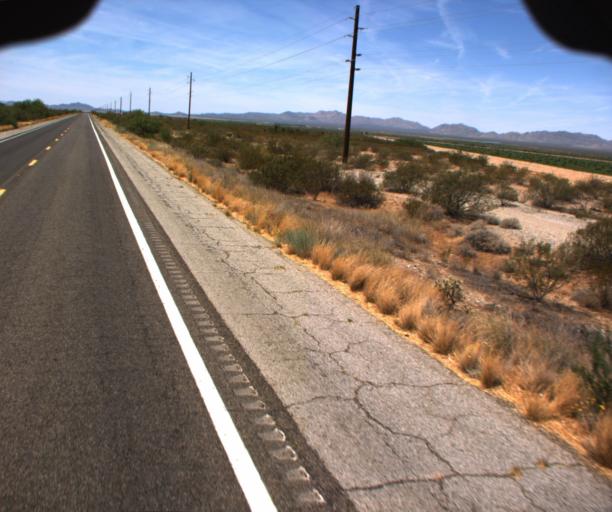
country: US
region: Arizona
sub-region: La Paz County
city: Salome
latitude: 33.8409
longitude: -113.4778
